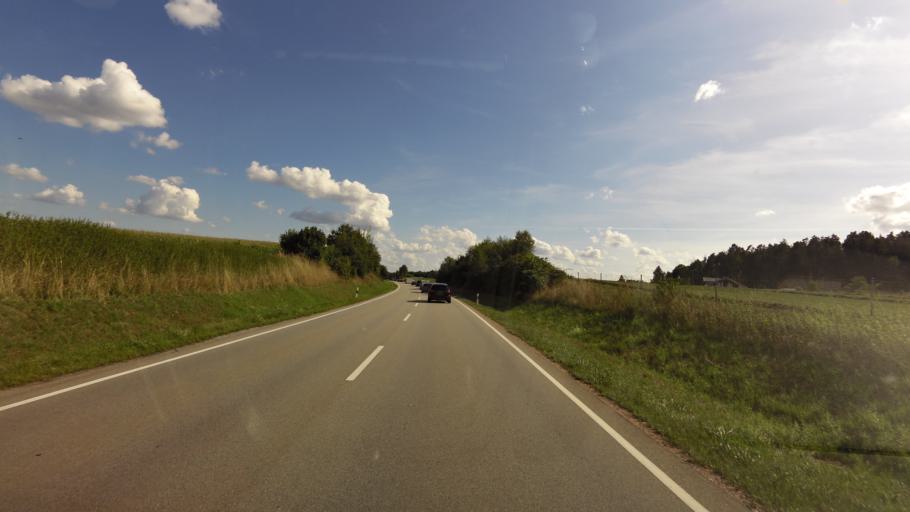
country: DE
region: Bavaria
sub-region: Lower Bavaria
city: Ascha
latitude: 48.9966
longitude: 12.6291
